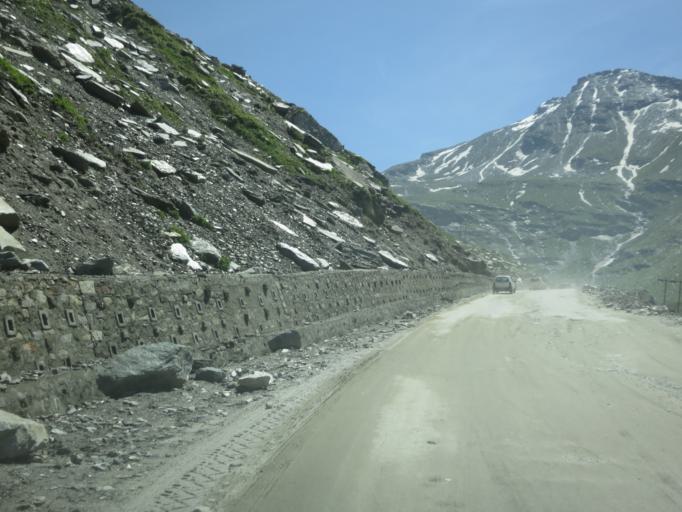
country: IN
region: Himachal Pradesh
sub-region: Kulu
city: Manali
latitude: 32.3560
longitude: 77.2270
